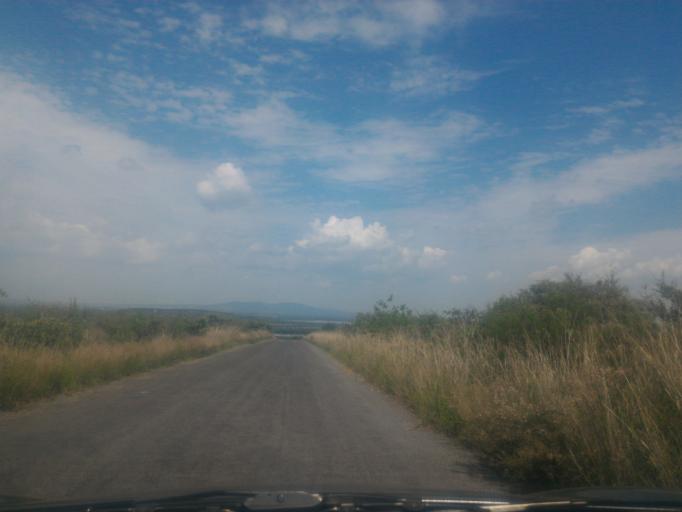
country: MX
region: Guanajuato
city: Ciudad Manuel Doblado
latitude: 20.8315
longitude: -102.0358
